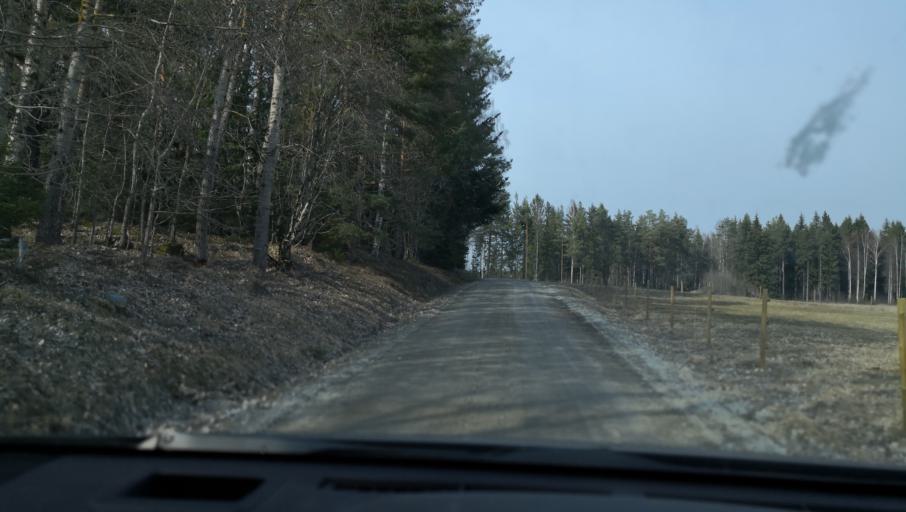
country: SE
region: OErebro
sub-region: Lindesbergs Kommun
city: Frovi
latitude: 59.3553
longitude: 15.4350
